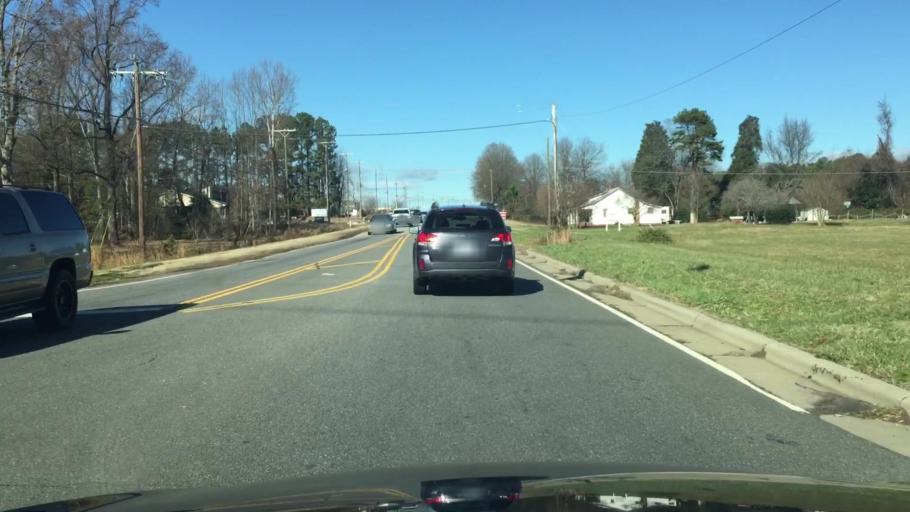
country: US
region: North Carolina
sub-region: Iredell County
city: Mooresville
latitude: 35.5782
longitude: -80.8713
